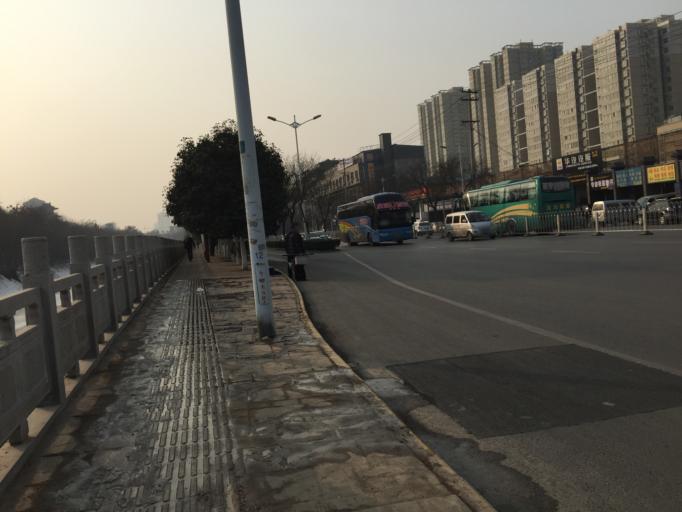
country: CN
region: Shaanxi
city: Weiyang
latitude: 34.2781
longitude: 108.9244
